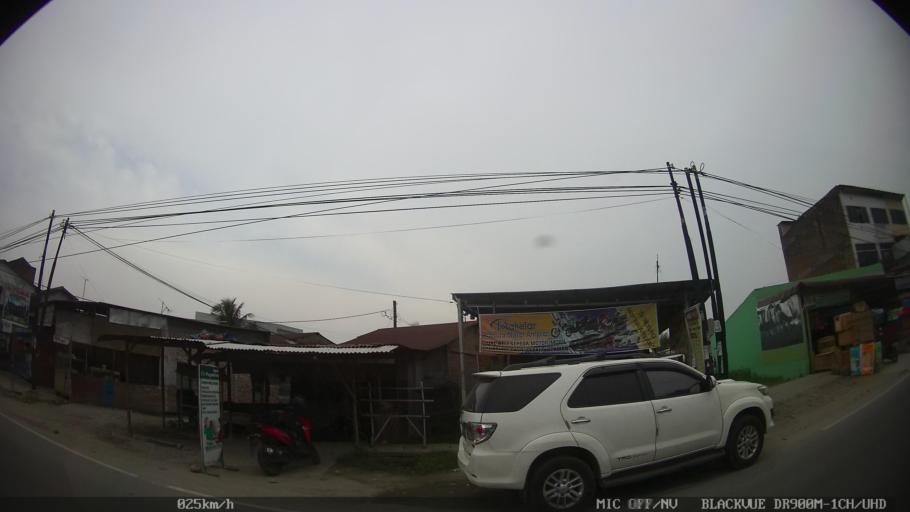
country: ID
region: North Sumatra
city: Deli Tua
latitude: 3.5482
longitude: 98.7163
